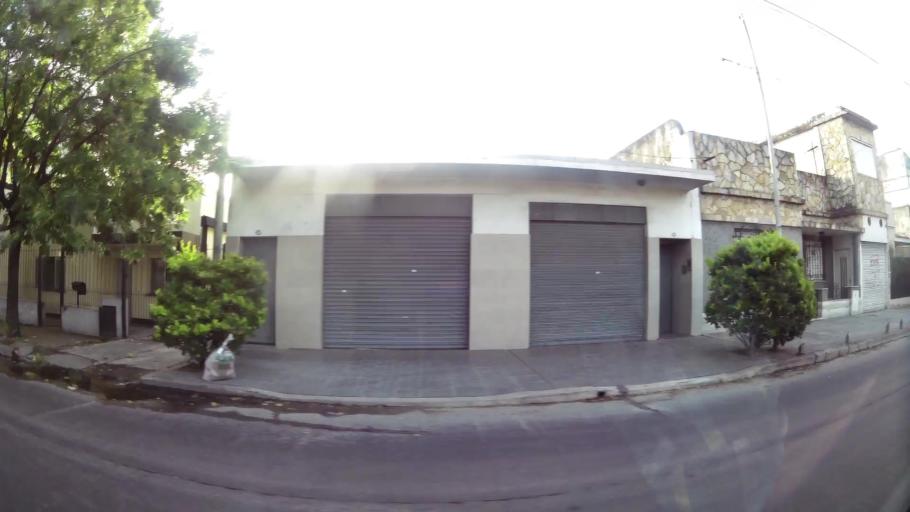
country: AR
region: Buenos Aires
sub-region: Partido de Moron
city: Moron
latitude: -34.6598
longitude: -58.6301
